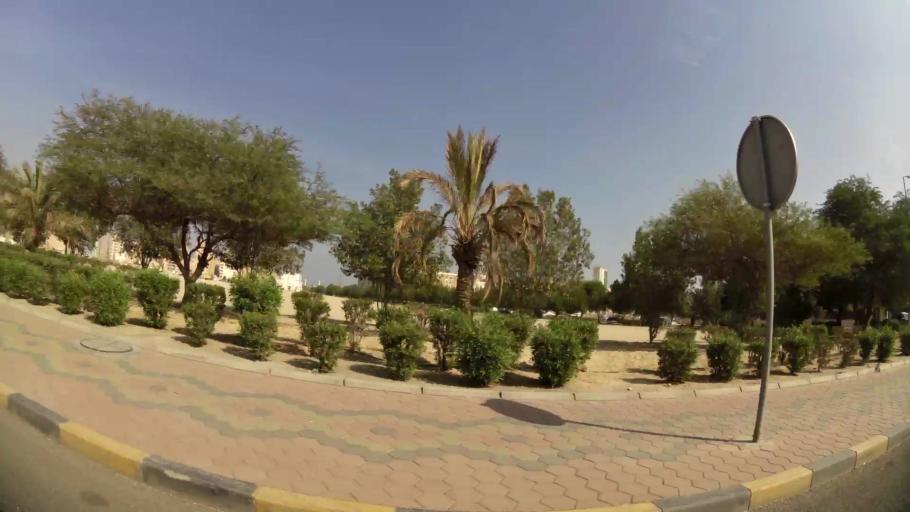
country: KW
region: Al Ahmadi
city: Al Fahahil
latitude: 29.0780
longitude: 48.1241
